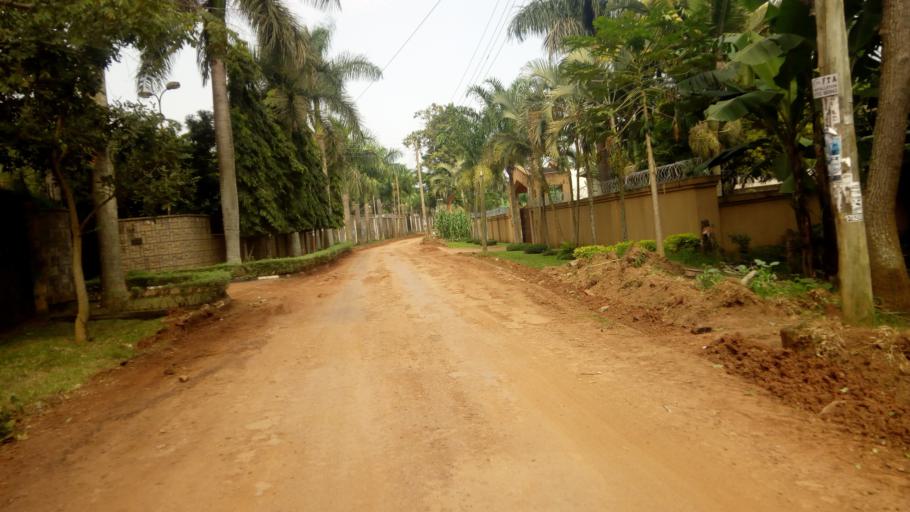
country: UG
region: Central Region
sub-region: Wakiso District
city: Kireka
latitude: 0.2910
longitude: 32.6594
